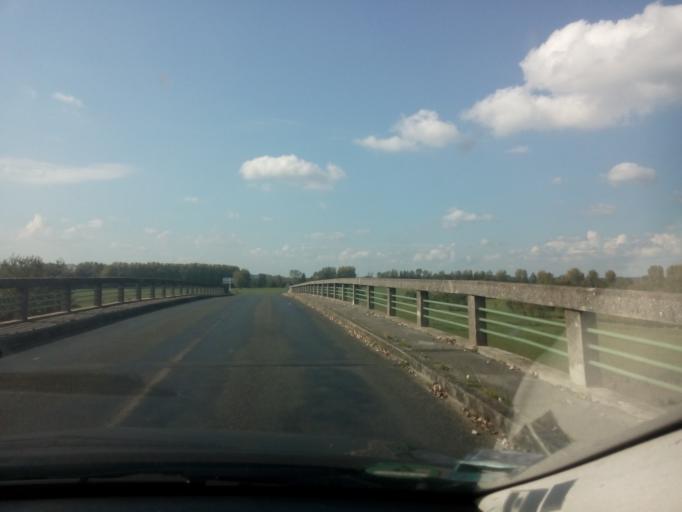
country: FR
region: Pays de la Loire
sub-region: Departement de Maine-et-Loire
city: Briollay
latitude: 47.5695
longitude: -0.5073
